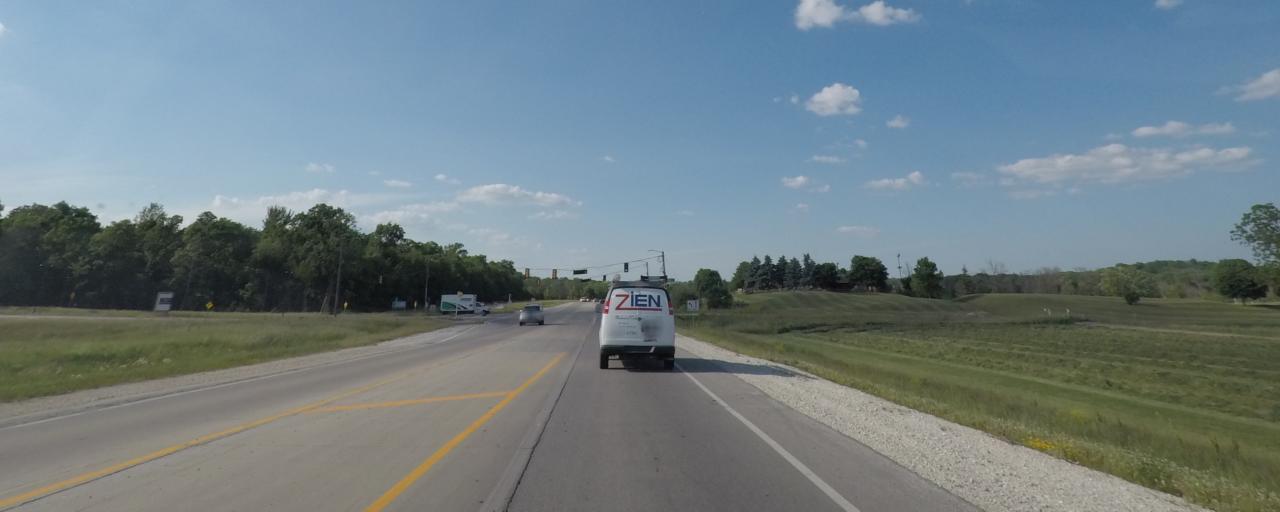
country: US
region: Wisconsin
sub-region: Waukesha County
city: Muskego
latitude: 42.9324
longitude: -88.1137
